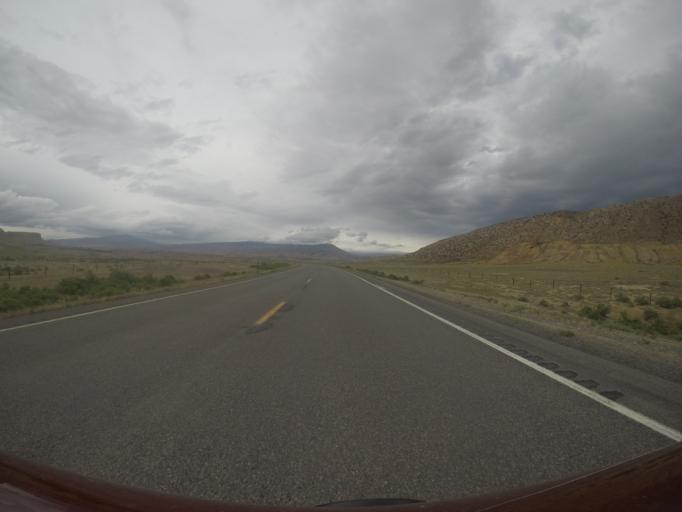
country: US
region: Wyoming
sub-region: Big Horn County
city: Lovell
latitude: 44.9385
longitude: -108.2967
